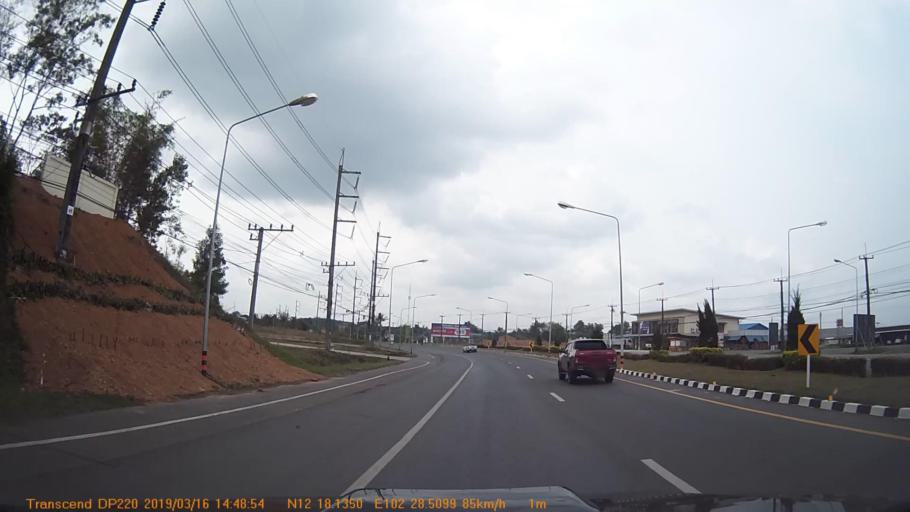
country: TH
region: Trat
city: Khao Saming
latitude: 12.3026
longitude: 102.4751
